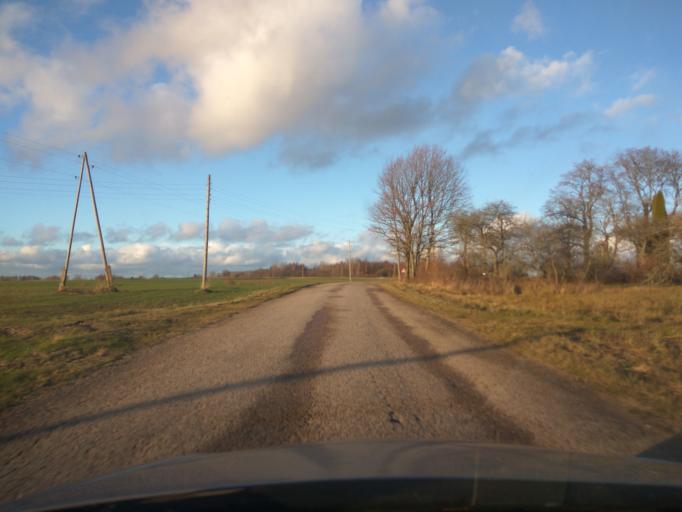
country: LV
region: Aizpute
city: Aizpute
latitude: 56.7702
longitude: 21.7846
